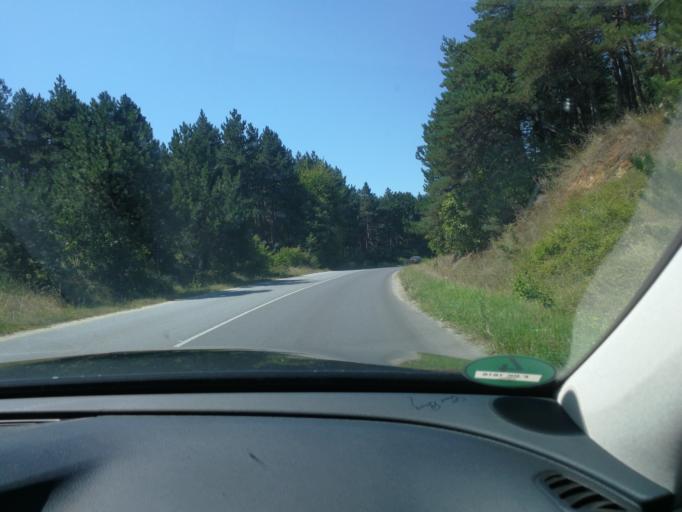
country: BG
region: Khaskovo
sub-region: Obshtina Topolovgrad
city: Topolovgrad
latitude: 42.0788
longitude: 26.3262
